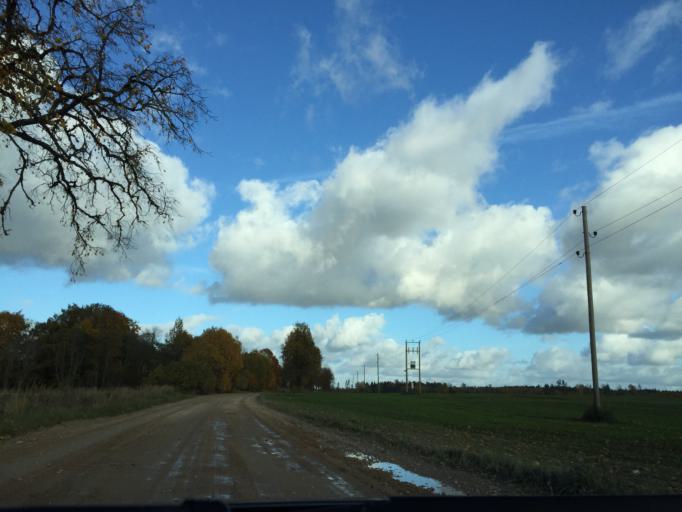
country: LV
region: Ogre
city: Jumprava
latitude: 56.7654
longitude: 24.9341
